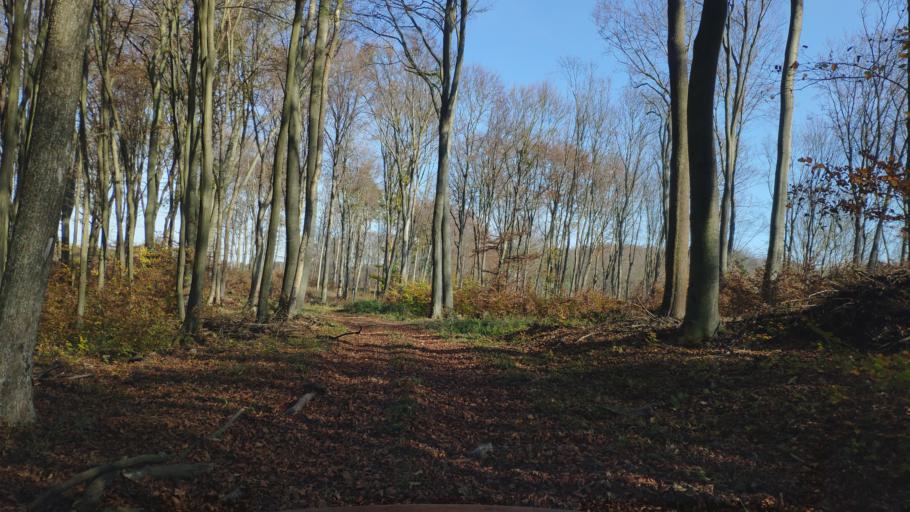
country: SK
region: Presovsky
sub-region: Okres Presov
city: Presov
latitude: 48.8956
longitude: 21.2102
